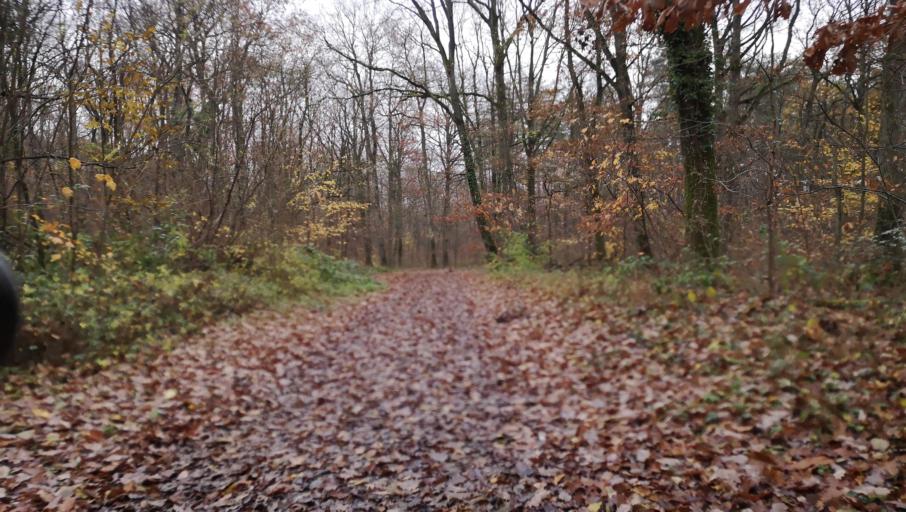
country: FR
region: Centre
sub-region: Departement du Loiret
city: Semoy
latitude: 47.9388
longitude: 1.9746
